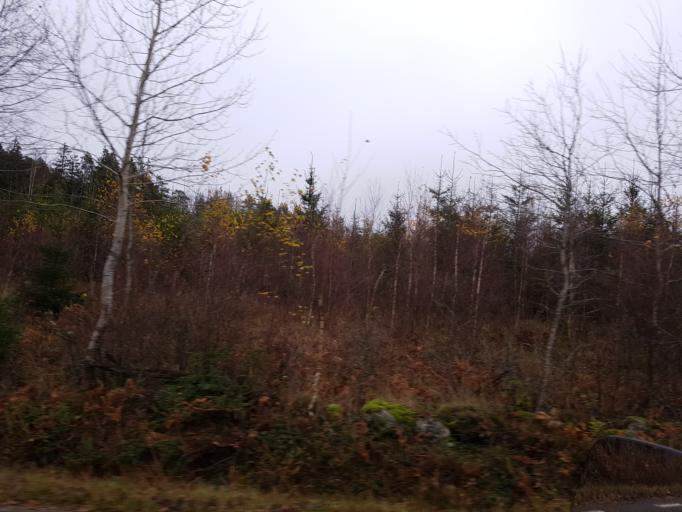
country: SE
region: Vaestra Goetaland
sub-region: Orust
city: Henan
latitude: 58.2132
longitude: 11.7721
